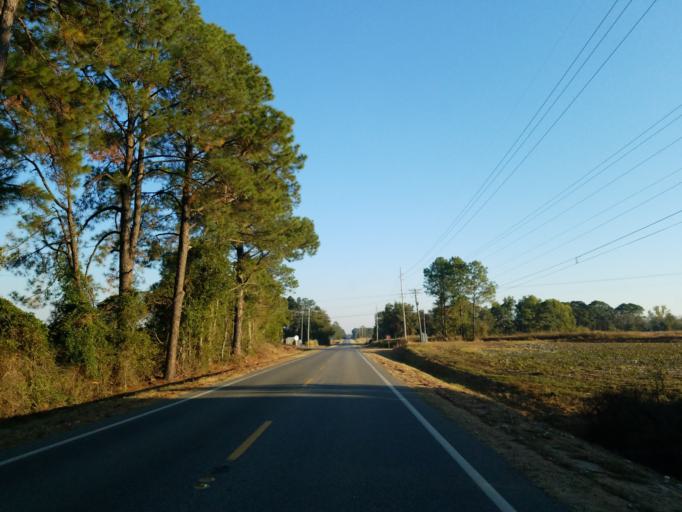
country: US
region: Georgia
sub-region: Crisp County
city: Cordele
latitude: 31.9012
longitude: -83.6961
